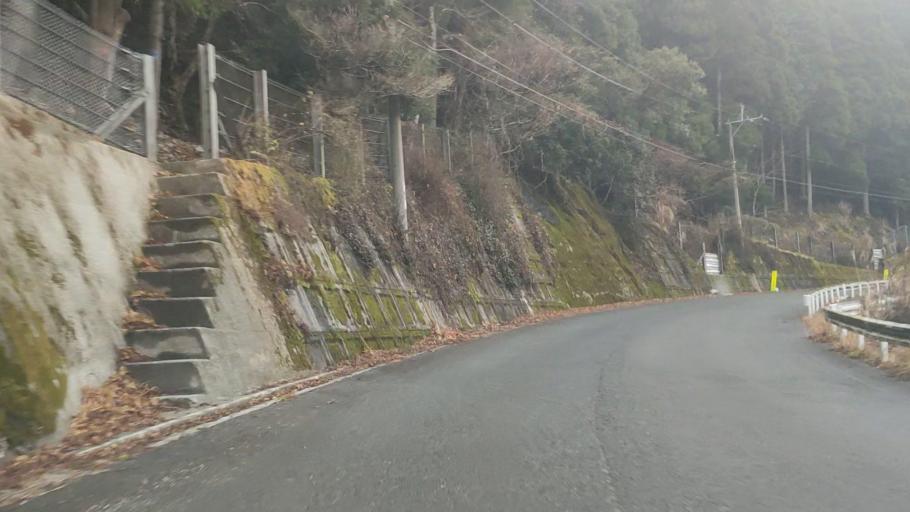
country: JP
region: Kumamoto
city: Matsubase
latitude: 32.6043
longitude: 130.8867
